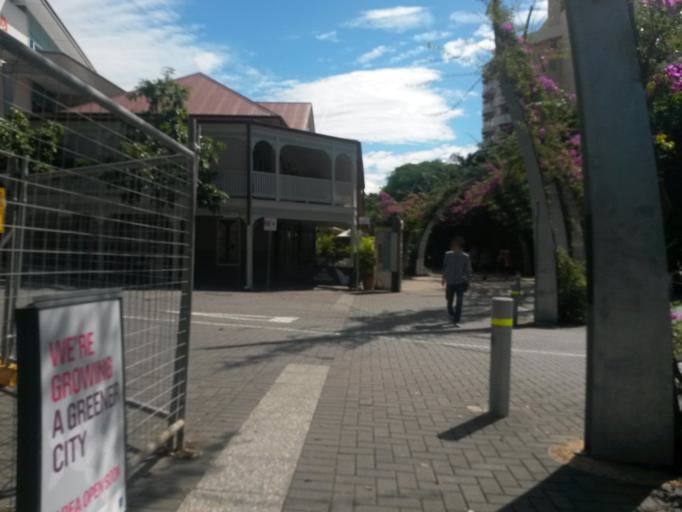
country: AU
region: Queensland
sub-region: Brisbane
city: South Brisbane
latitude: -27.4823
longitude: 153.0253
